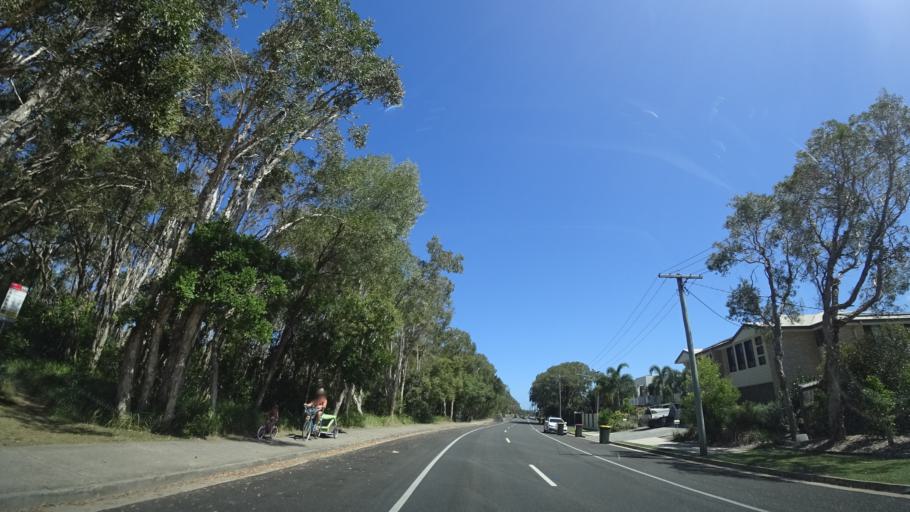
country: AU
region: Queensland
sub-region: Sunshine Coast
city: Mooloolaba
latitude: -26.6126
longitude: 153.0999
